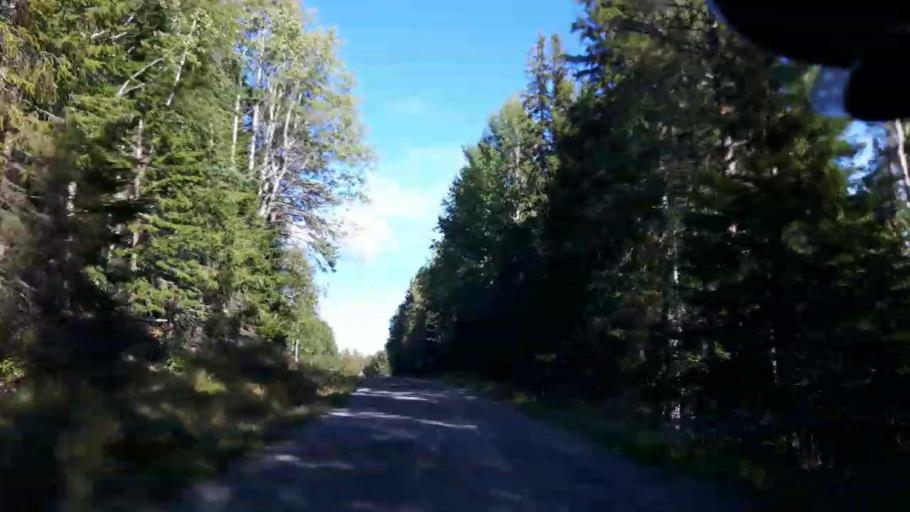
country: SE
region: Jaemtland
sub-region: Ragunda Kommun
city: Hammarstrand
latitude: 63.5281
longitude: 16.0737
